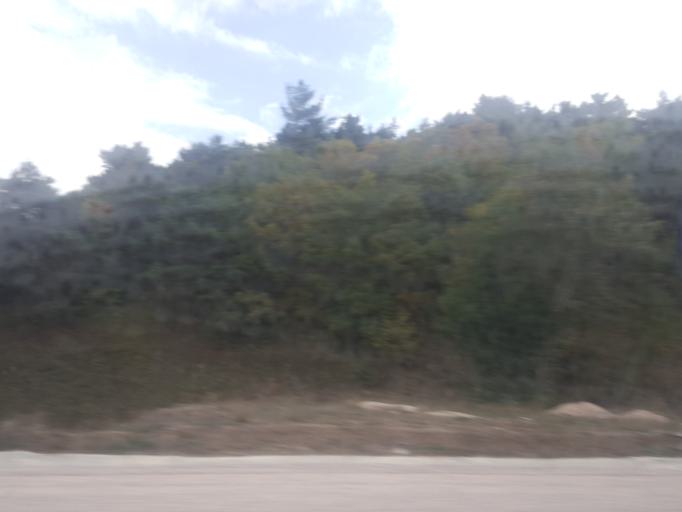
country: TR
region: Tokat
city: Bereketli
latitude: 40.5363
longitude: 37.3094
